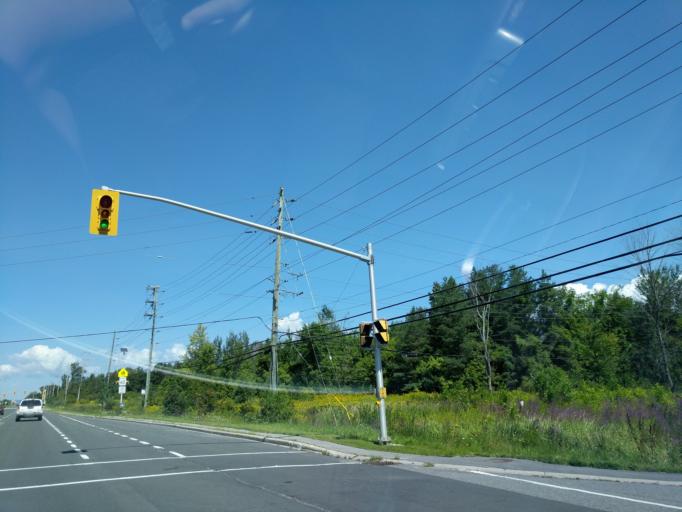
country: CA
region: Ontario
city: Bells Corners
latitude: 45.3456
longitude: -75.8435
